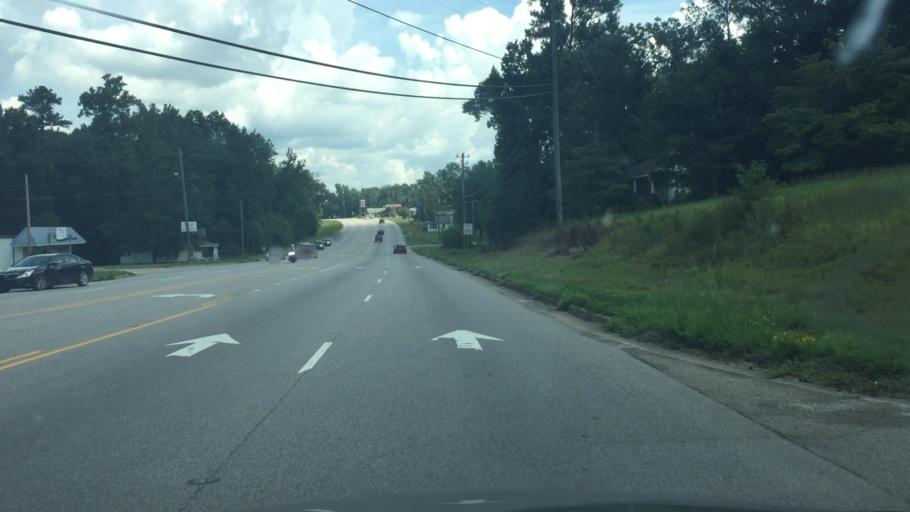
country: US
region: North Carolina
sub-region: Richmond County
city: East Rockingham
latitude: 34.9148
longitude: -79.7878
